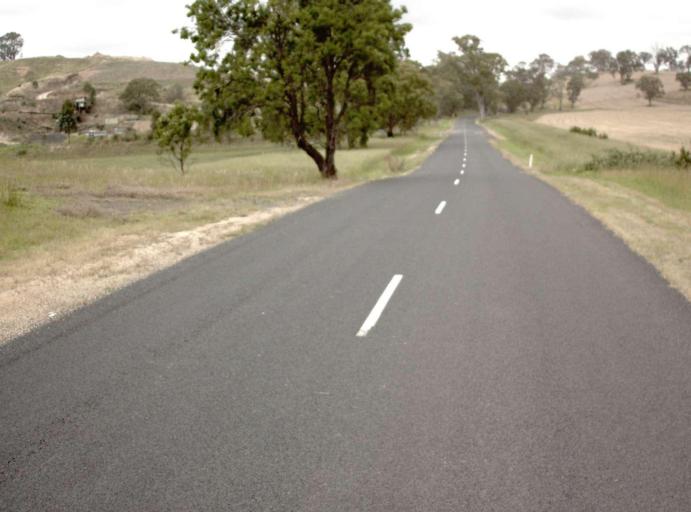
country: AU
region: Victoria
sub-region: Wellington
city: Heyfield
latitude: -37.8911
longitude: 146.7249
